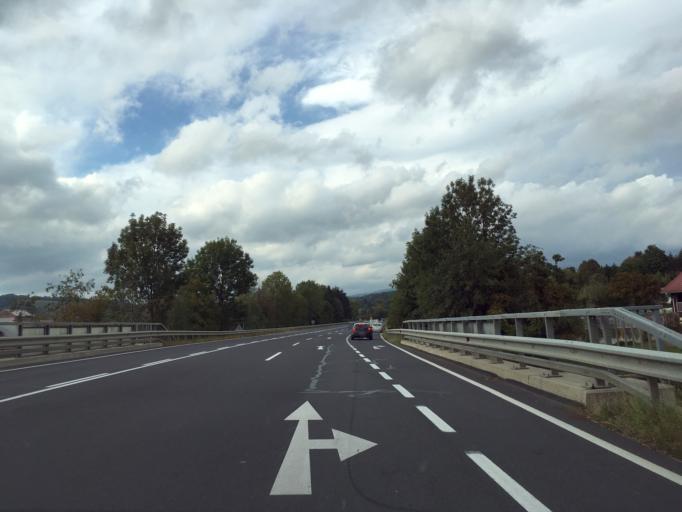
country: AT
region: Styria
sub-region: Politischer Bezirk Hartberg-Fuerstenfeld
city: Rohrbach an der Lafnitz
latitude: 47.3863
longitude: 16.0036
